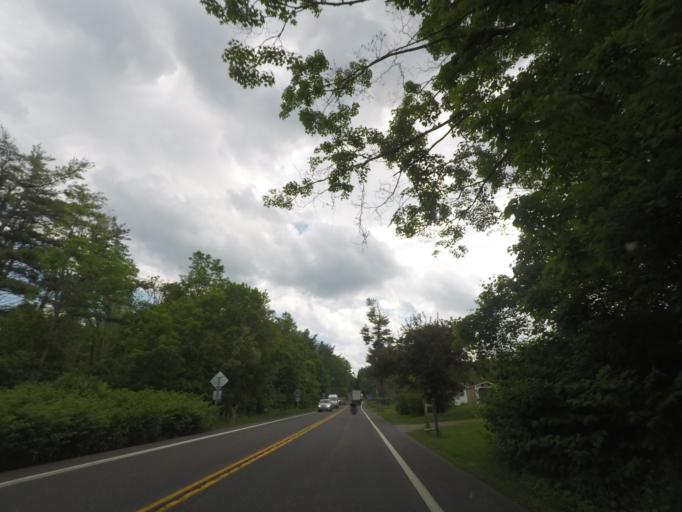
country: US
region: New York
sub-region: Dutchess County
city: Pine Plains
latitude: 42.0784
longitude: -73.6723
